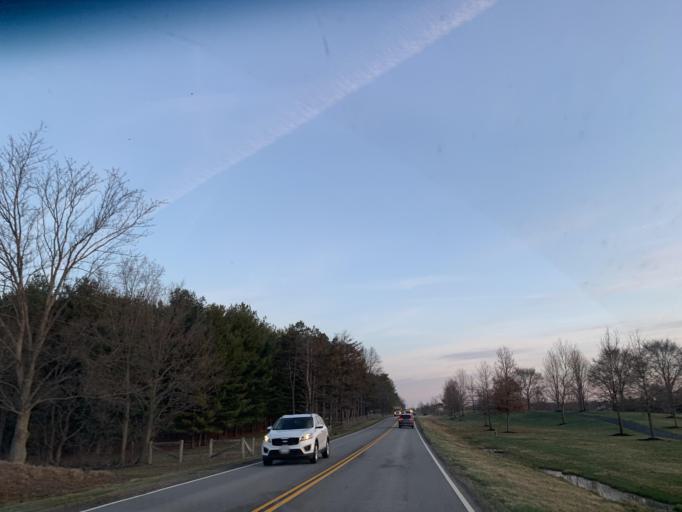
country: US
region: Ohio
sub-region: Union County
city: New California
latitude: 40.1437
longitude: -83.1818
